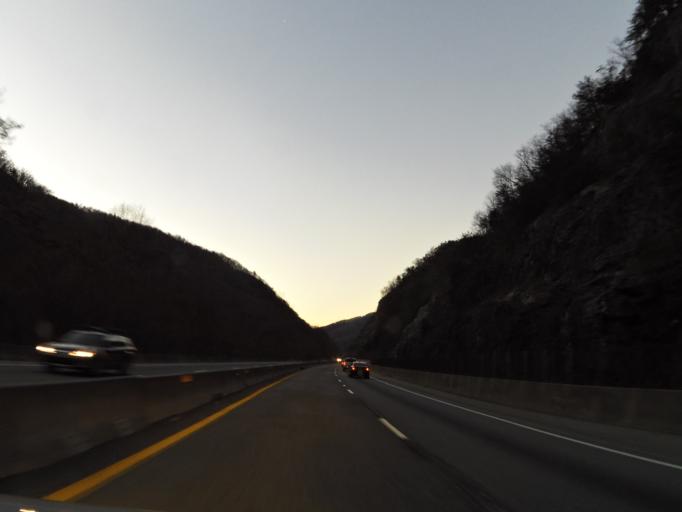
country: US
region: North Carolina
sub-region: Haywood County
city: Cove Creek
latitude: 35.7516
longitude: -83.0660
